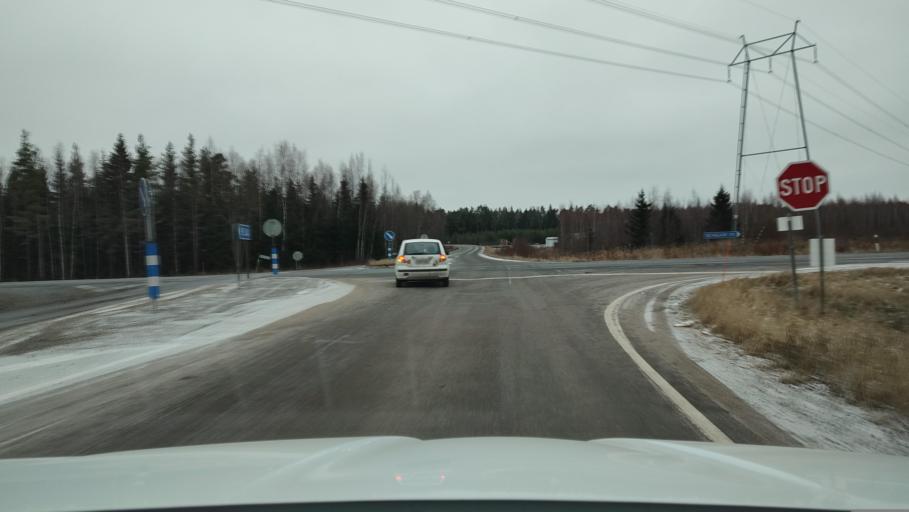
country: FI
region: Ostrobothnia
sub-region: Sydosterbotten
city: Naerpes
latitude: 62.3986
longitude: 21.3663
